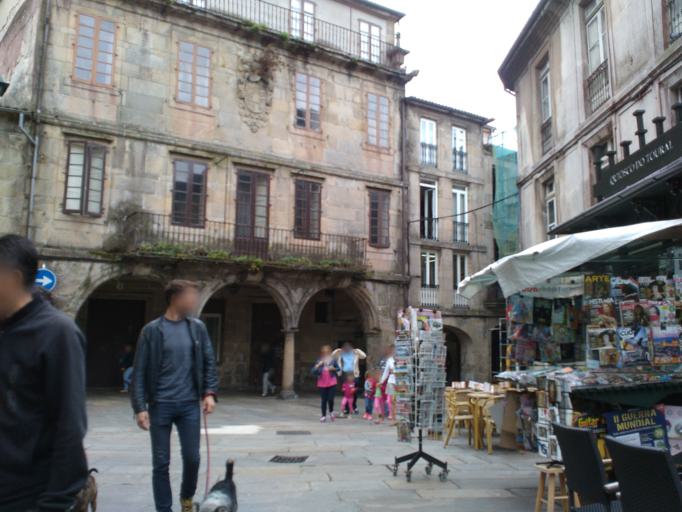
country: ES
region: Galicia
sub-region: Provincia da Coruna
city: Santiago de Compostela
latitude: 42.8778
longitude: -8.5441
